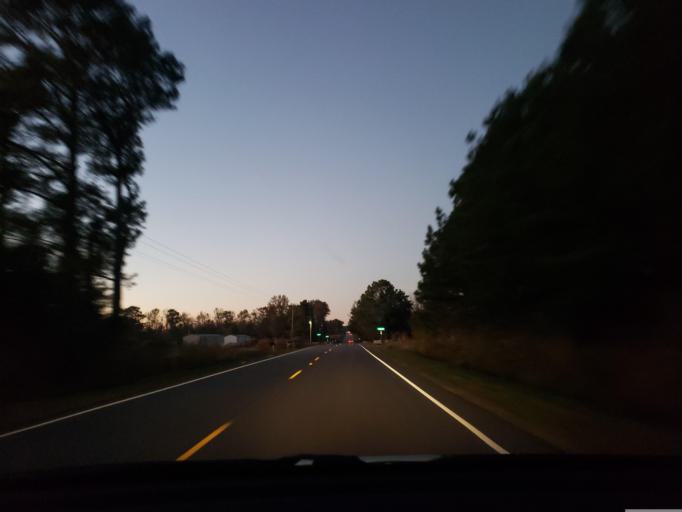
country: US
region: North Carolina
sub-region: Duplin County
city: Kenansville
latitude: 34.9278
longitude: -77.9387
